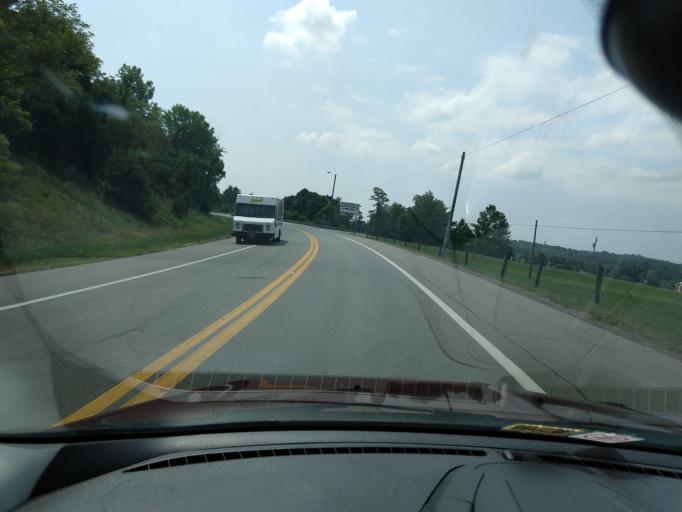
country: US
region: West Virginia
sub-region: Jackson County
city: Ravenswood
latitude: 38.8612
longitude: -81.8192
